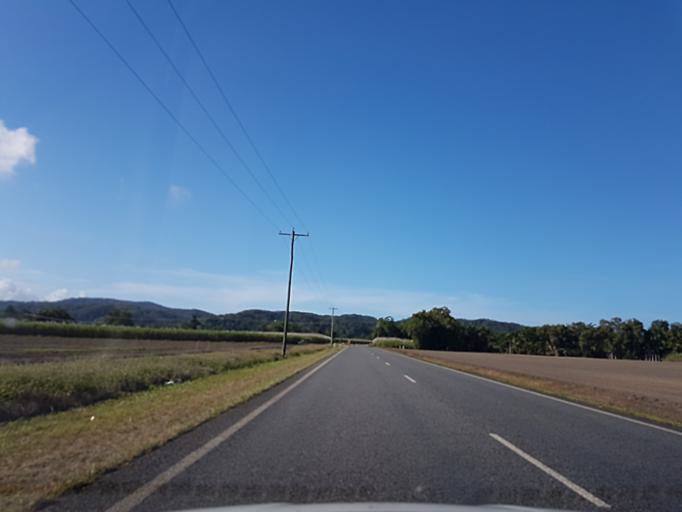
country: AU
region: Queensland
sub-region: Cairns
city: Port Douglas
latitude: -16.3959
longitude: 145.3859
